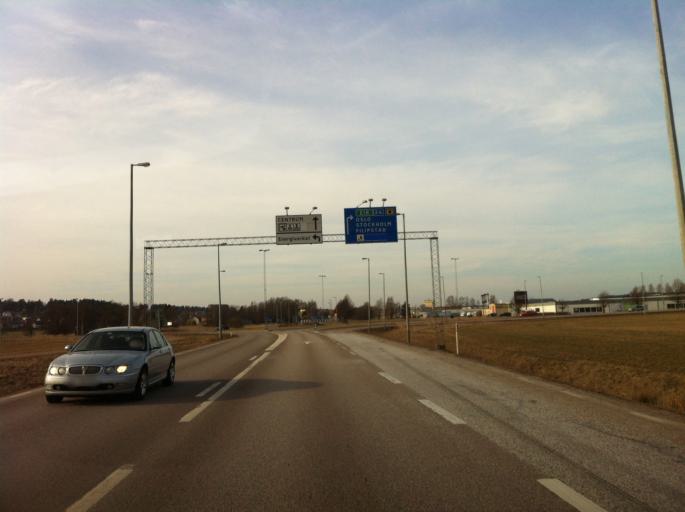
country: SE
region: Vaermland
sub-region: Kristinehamns Kommun
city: Kristinehamn
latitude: 59.2943
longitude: 14.1256
